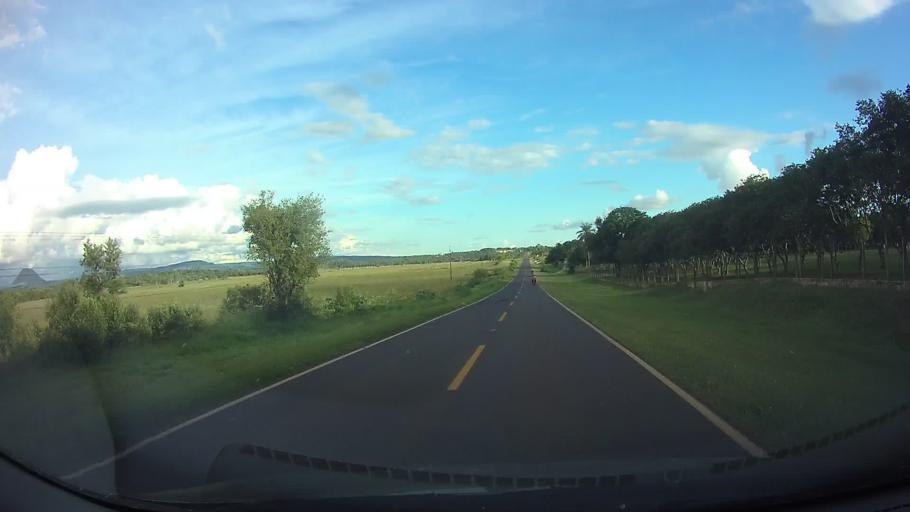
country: PY
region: Paraguari
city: Ybycui
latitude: -25.9967
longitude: -57.0507
